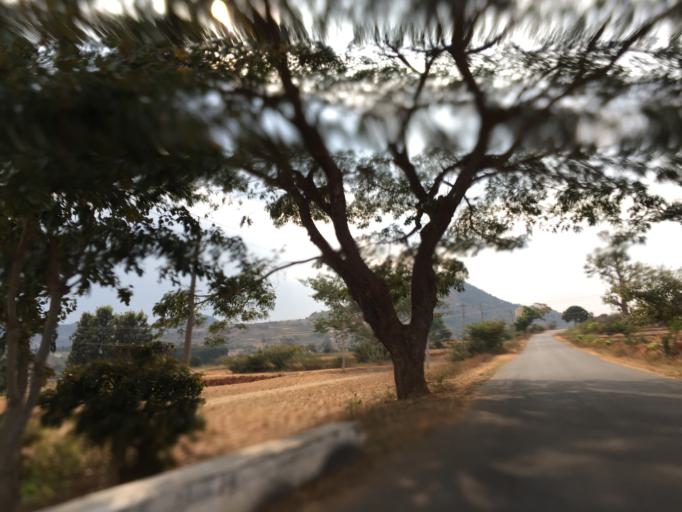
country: IN
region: Karnataka
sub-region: Chikkaballapur
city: Chik Ballapur
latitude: 13.5521
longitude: 77.7515
